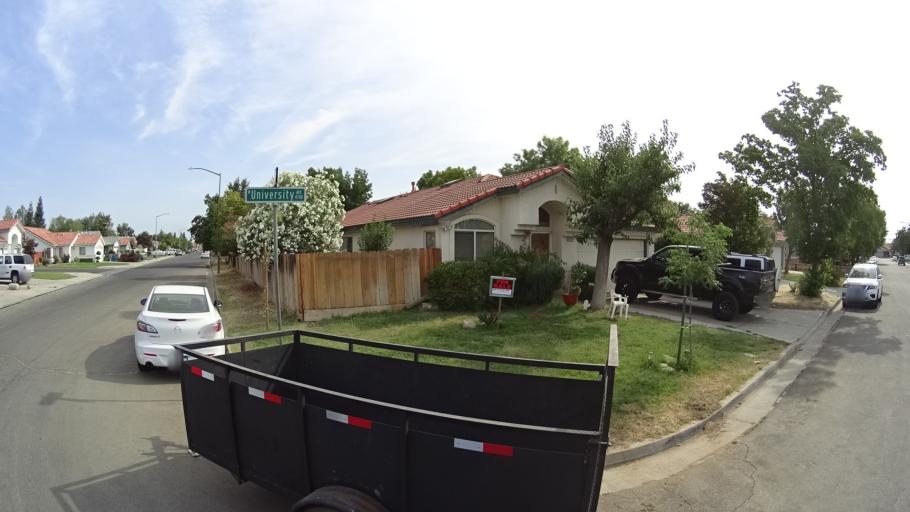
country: US
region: California
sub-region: Fresno County
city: West Park
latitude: 36.7667
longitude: -119.8783
